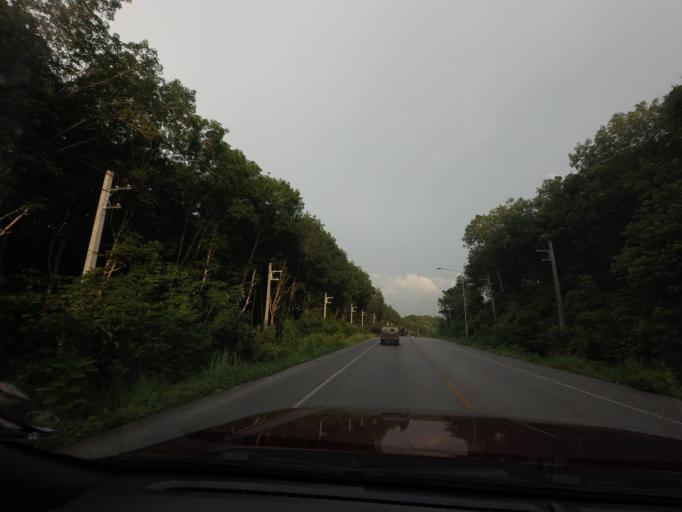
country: TH
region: Pattani
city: Mae Lan
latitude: 6.6716
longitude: 101.1575
